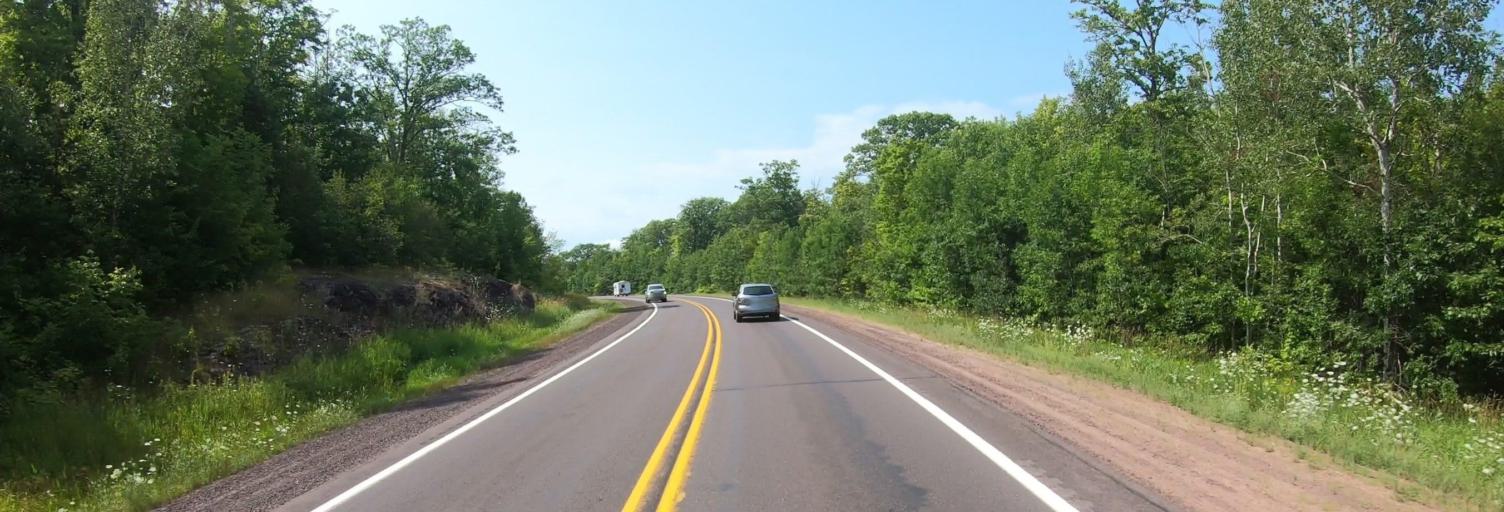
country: US
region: Michigan
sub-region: Ontonagon County
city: Ontonagon
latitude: 46.8604
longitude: -88.9375
